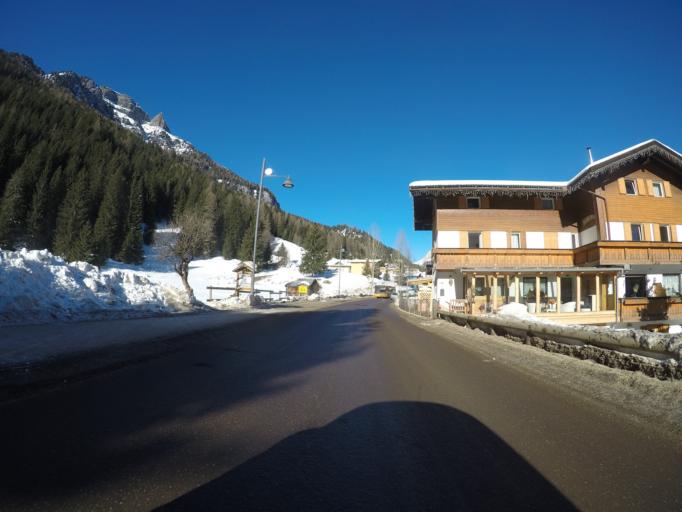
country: IT
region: Trentino-Alto Adige
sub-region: Provincia di Trento
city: Canazei
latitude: 46.4597
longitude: 11.7853
